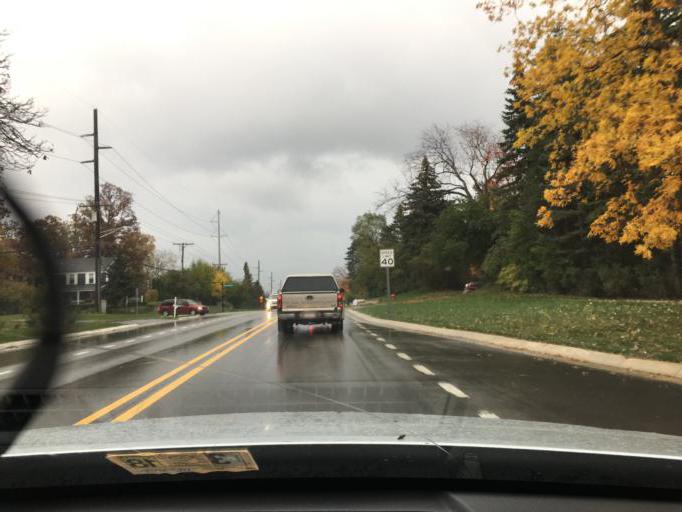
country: US
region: Michigan
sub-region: Oakland County
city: Rochester
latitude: 42.6950
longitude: -83.1639
